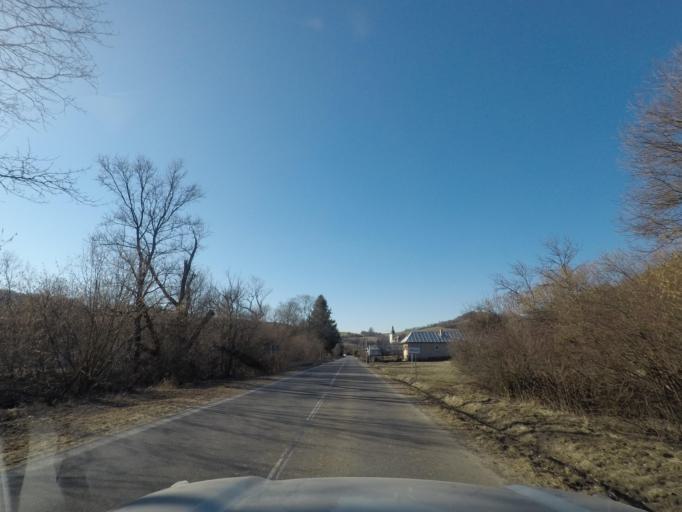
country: PL
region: Subcarpathian Voivodeship
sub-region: Powiat sanocki
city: Komancza
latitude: 49.1617
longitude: 22.0442
